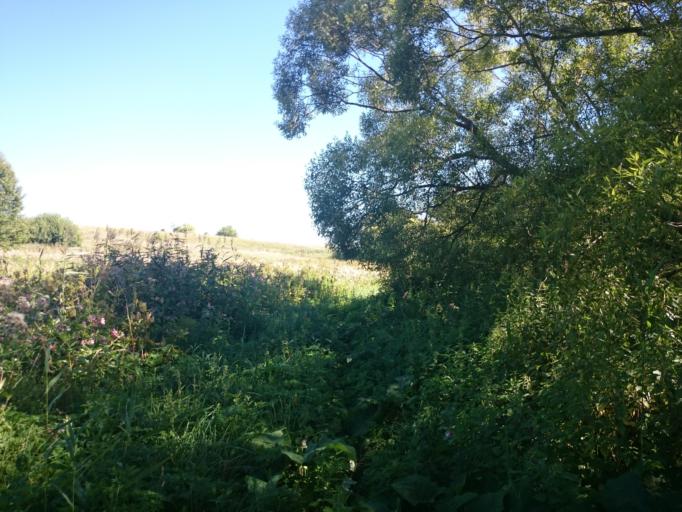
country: RU
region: Mordoviya
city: Kadoshkino
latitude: 54.0324
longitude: 44.4934
